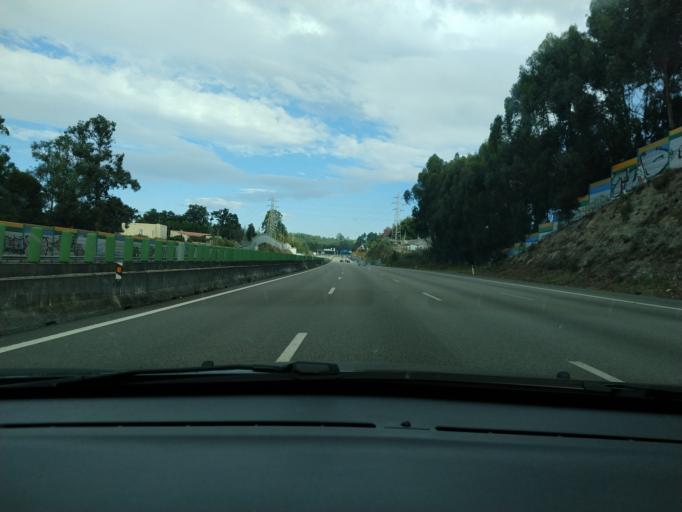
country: PT
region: Porto
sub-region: Vila Nova de Gaia
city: Perozinho
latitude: 41.0611
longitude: -8.5790
